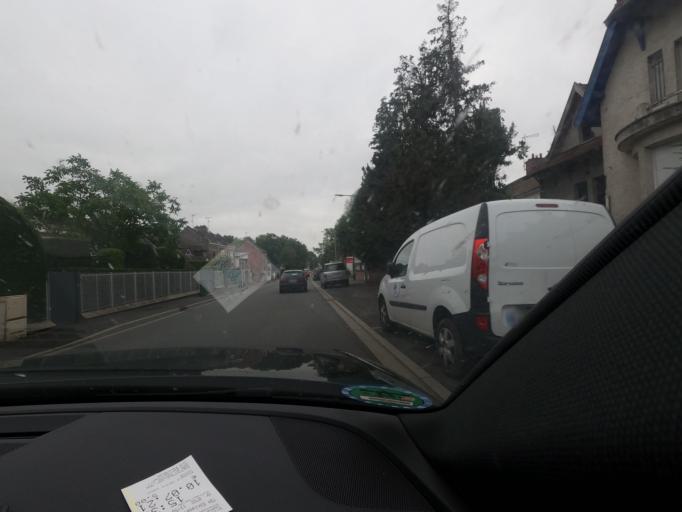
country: FR
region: Picardie
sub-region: Departement de la Somme
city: Amiens
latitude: 49.8756
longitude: 2.3062
